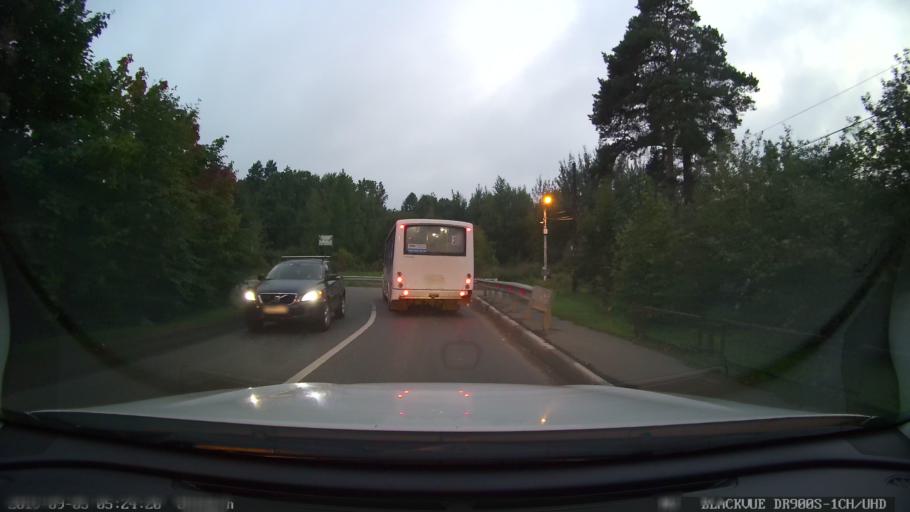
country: RU
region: Moskovskaya
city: Levoberezhnaya
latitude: 55.9202
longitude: 37.4686
